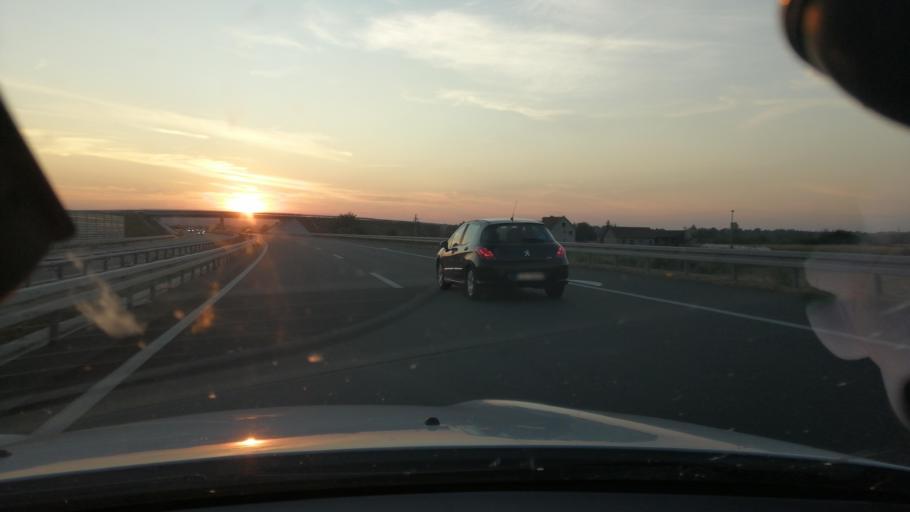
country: RS
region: Central Serbia
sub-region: Kolubarski Okrug
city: Lajkovac
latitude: 44.3443
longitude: 20.1803
